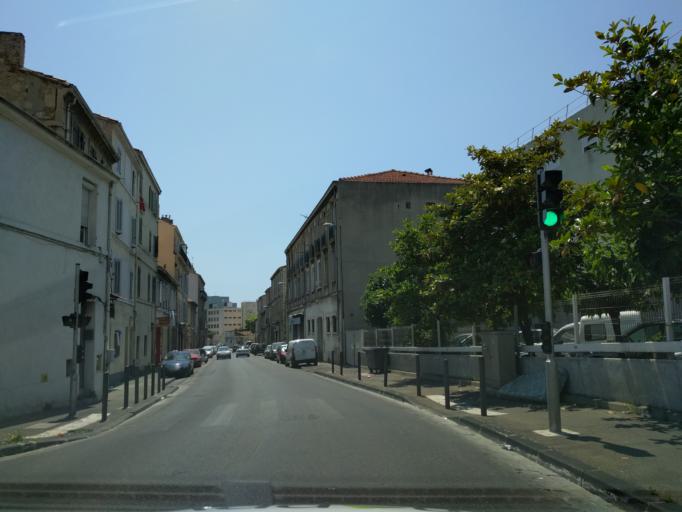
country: FR
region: Provence-Alpes-Cote d'Azur
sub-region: Departement des Bouches-du-Rhone
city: Marseille 14
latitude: 43.3303
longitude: 5.3590
